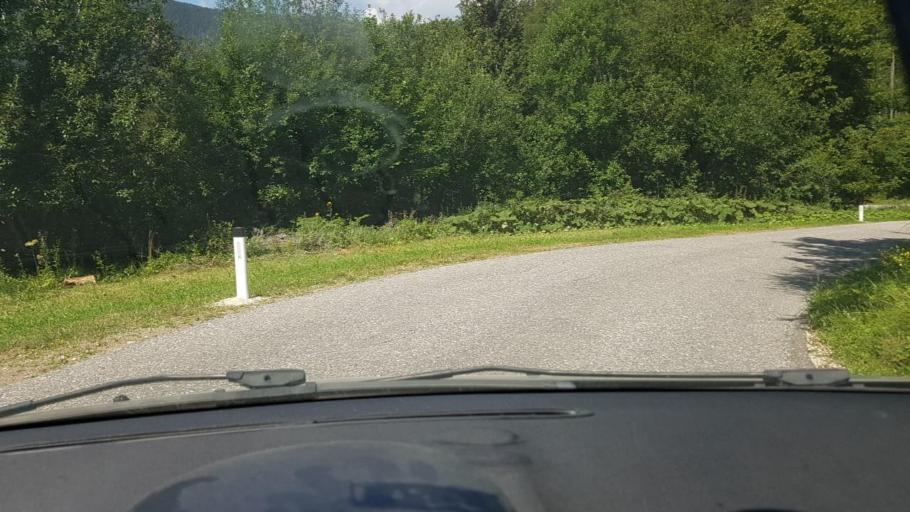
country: SI
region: Jezersko
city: Zgornje Jezersko
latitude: 46.4197
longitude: 14.5591
